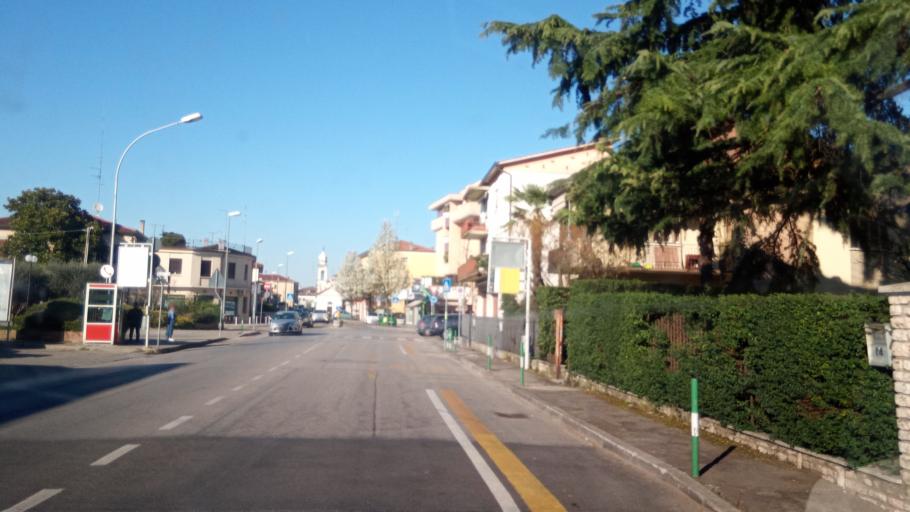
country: IT
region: Veneto
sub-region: Provincia di Padova
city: Cadoneghe
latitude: 45.4230
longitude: 11.9109
